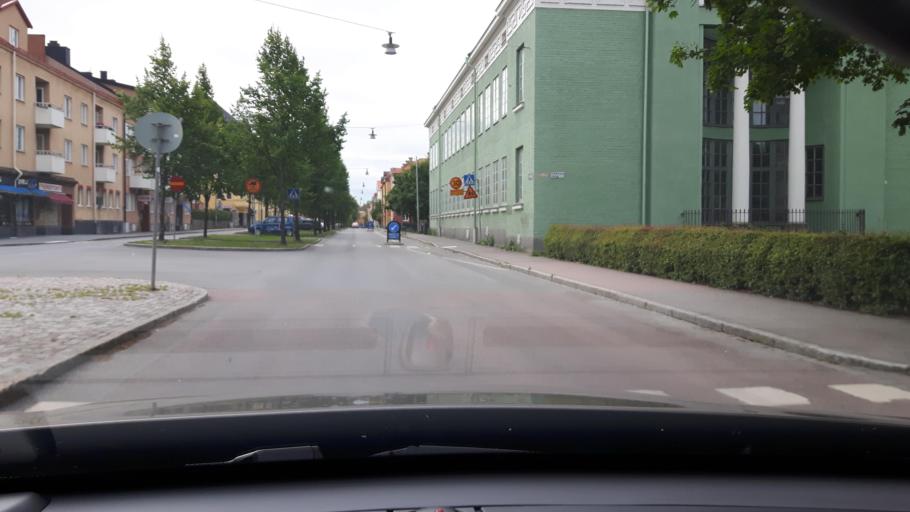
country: SE
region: Uppsala
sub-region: Uppsala Kommun
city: Uppsala
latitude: 59.8618
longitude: 17.6480
